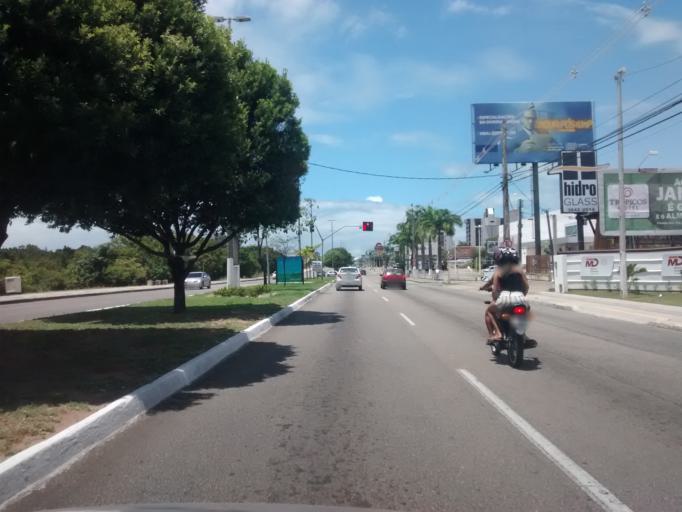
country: BR
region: Rio Grande do Norte
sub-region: Natal
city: Natal
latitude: -5.8603
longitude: -35.1931
